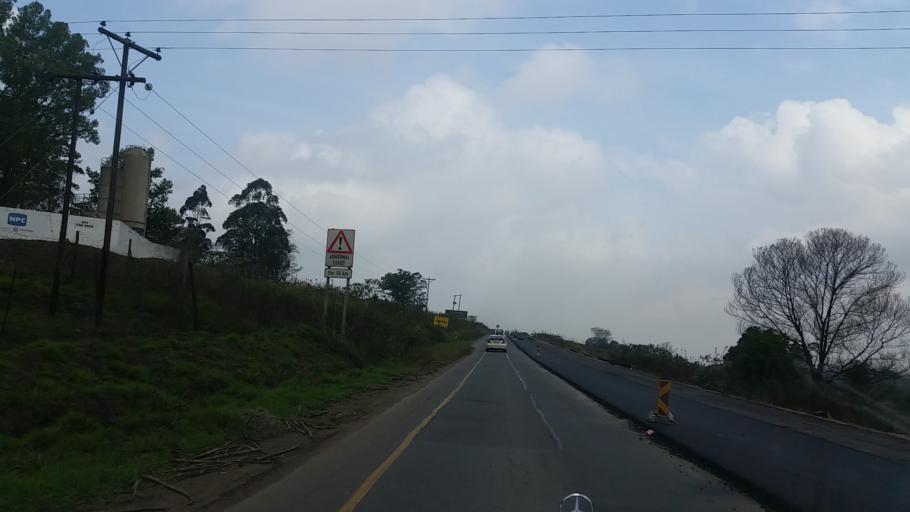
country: ZA
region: KwaZulu-Natal
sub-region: uMgungundlovu District Municipality
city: Camperdown
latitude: -29.7316
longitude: 30.5048
